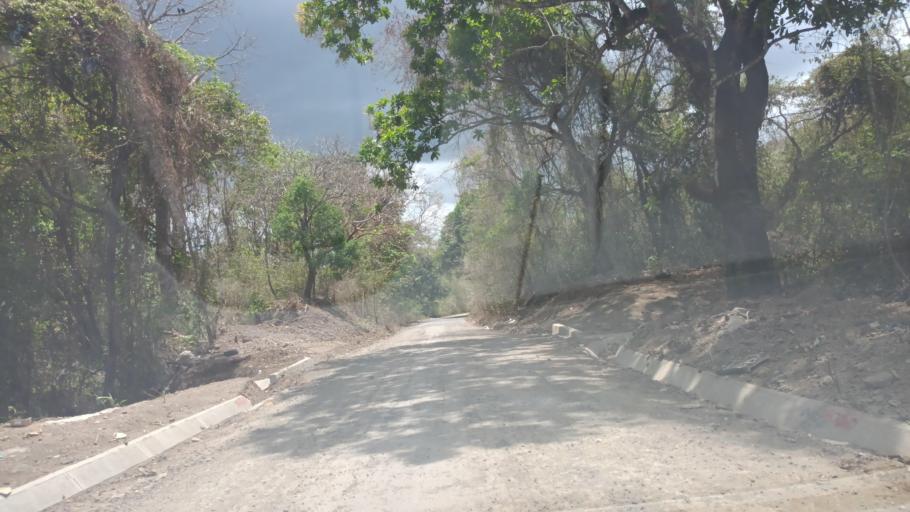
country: PA
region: Panama
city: Las Cumbres
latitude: 9.0615
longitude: -79.5663
